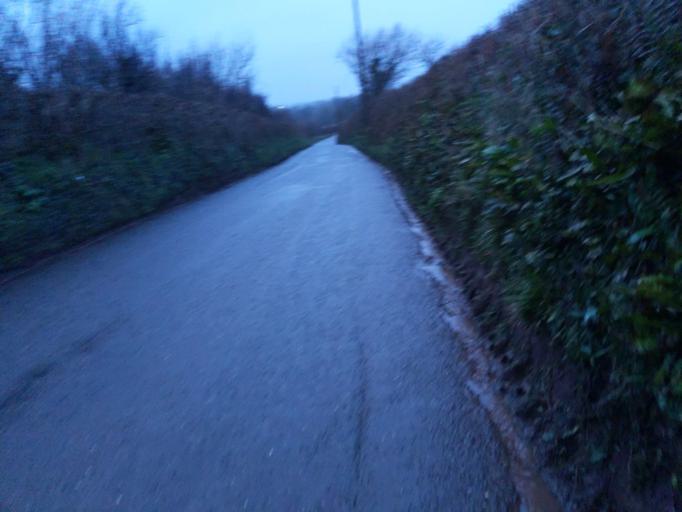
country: GB
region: England
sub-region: Devon
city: Yealmpton
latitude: 50.3343
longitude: -4.0139
